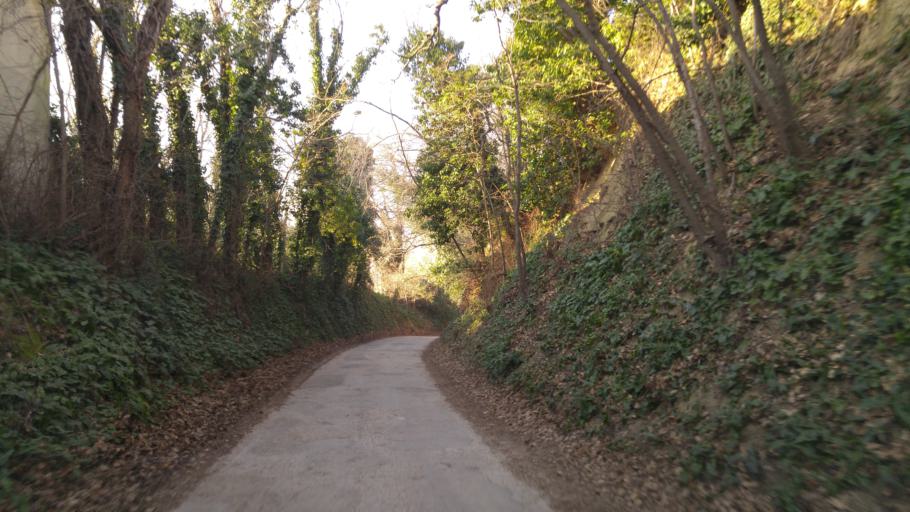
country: IT
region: The Marches
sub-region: Provincia di Pesaro e Urbino
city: Fenile
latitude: 43.8607
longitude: 12.9660
